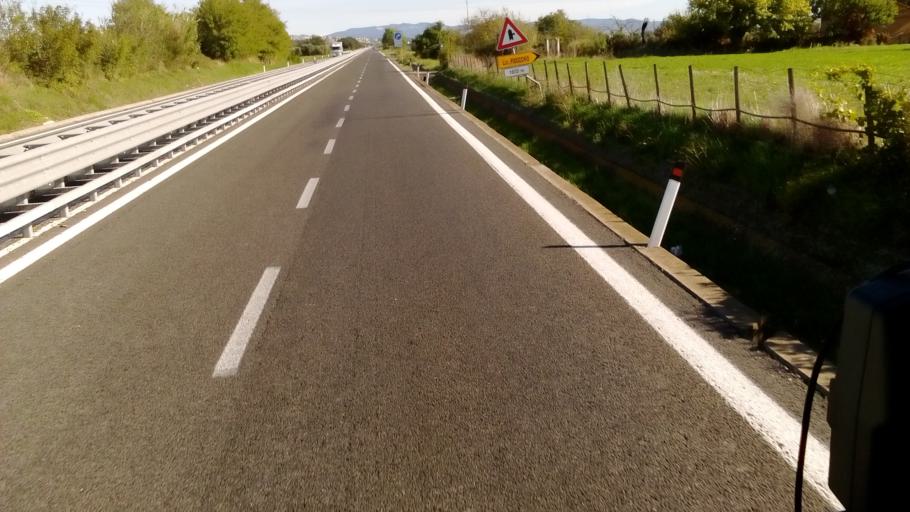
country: IT
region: Latium
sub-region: Provincia di Viterbo
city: Tarquinia
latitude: 42.2810
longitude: 11.6953
